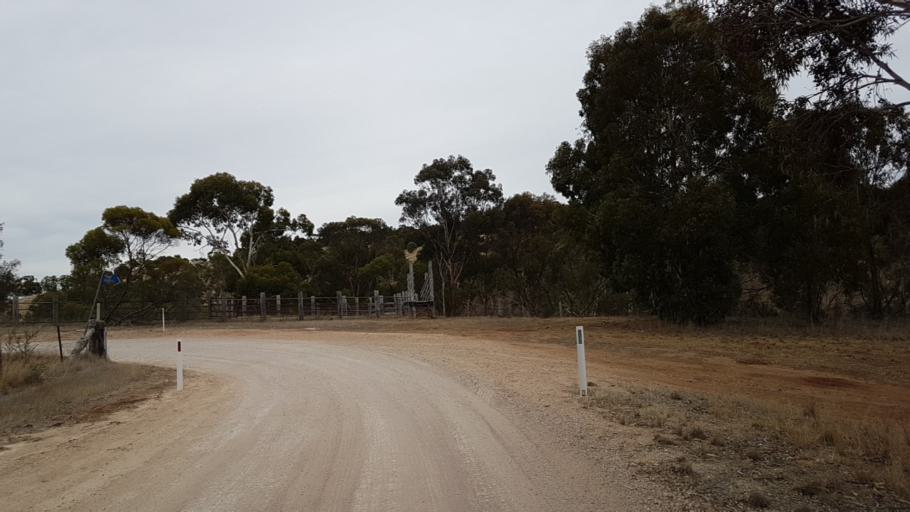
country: AU
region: South Australia
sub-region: Mount Barker
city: Callington
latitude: -35.0061
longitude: 139.0323
